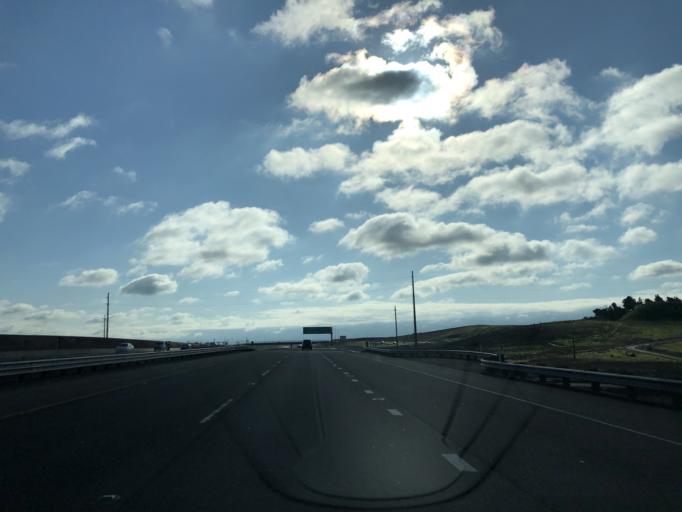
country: US
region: California
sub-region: Contra Costa County
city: Oakley
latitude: 37.9846
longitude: -121.7485
